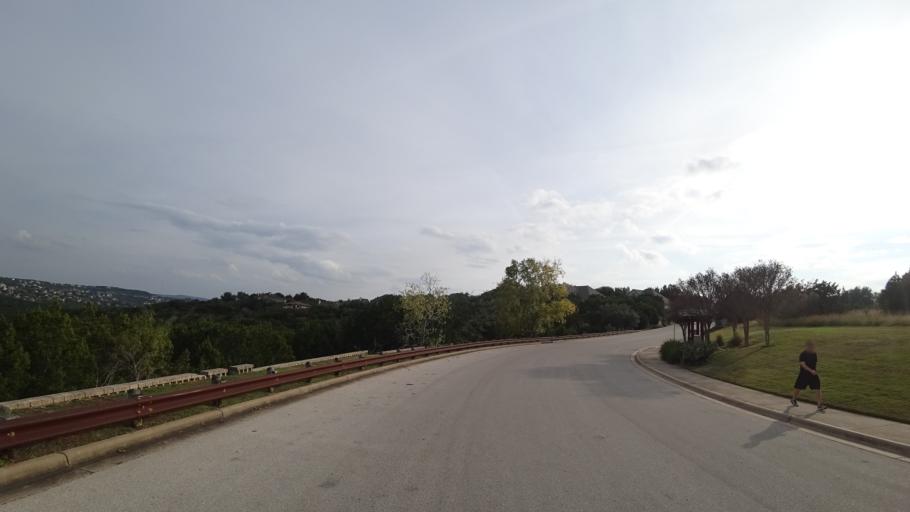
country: US
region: Texas
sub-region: Travis County
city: Hudson Bend
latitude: 30.3774
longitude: -97.8797
